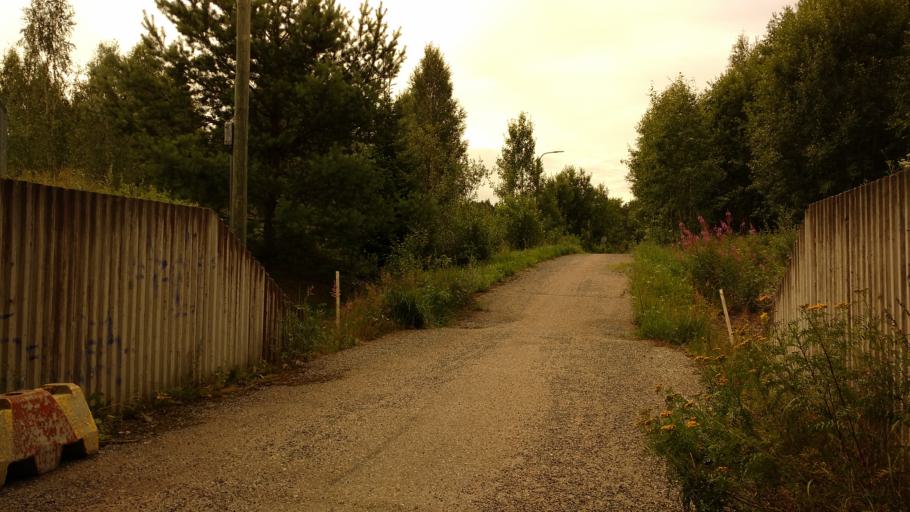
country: FI
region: Varsinais-Suomi
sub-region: Turku
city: Lieto
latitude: 60.4434
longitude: 22.4328
